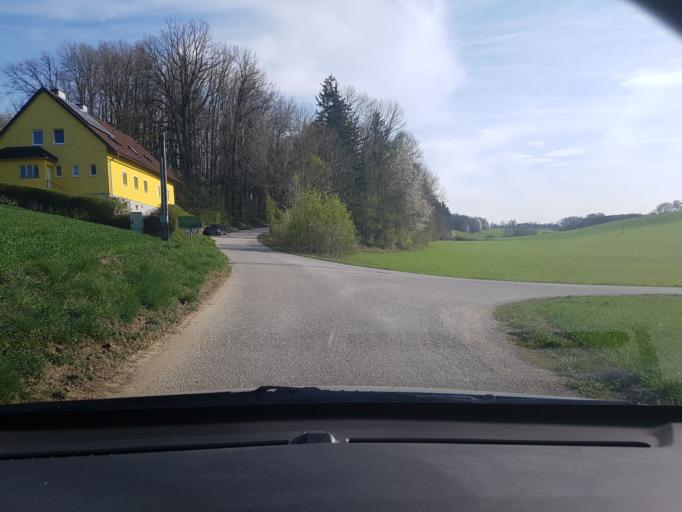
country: AT
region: Upper Austria
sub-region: Politischer Bezirk Linz-Land
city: Ansfelden
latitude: 48.1768
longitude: 14.3295
